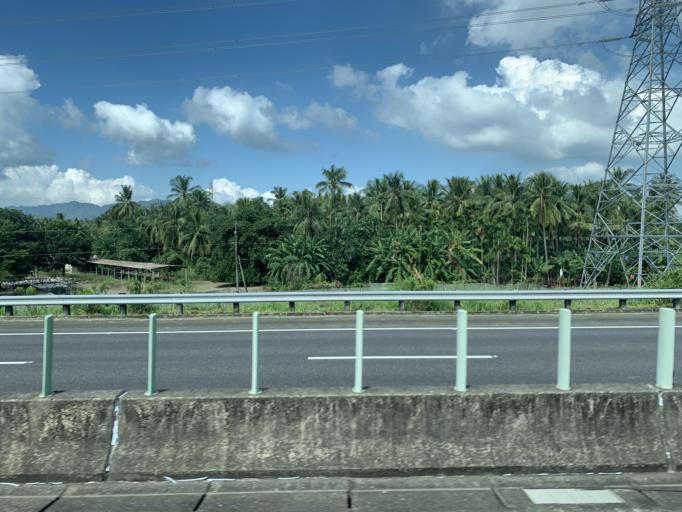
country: TW
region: Taiwan
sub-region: Pingtung
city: Pingtung
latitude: 22.8381
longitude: 120.4951
